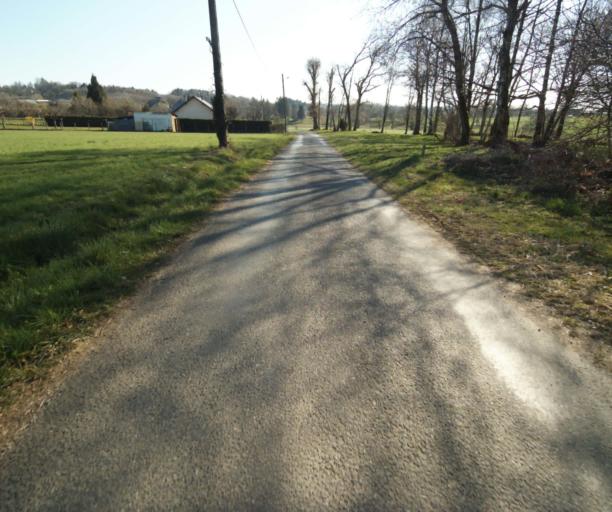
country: FR
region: Limousin
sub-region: Departement de la Correze
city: Chamboulive
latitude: 45.4753
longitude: 1.7249
